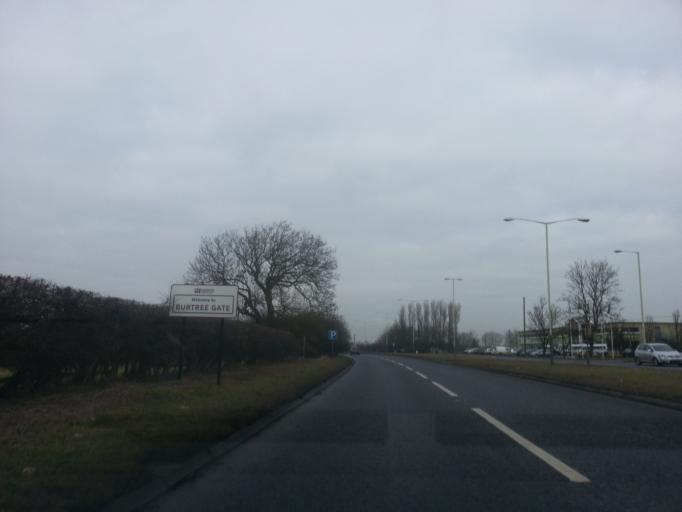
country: GB
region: England
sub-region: Darlington
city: Heighington
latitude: 54.5614
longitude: -1.5969
